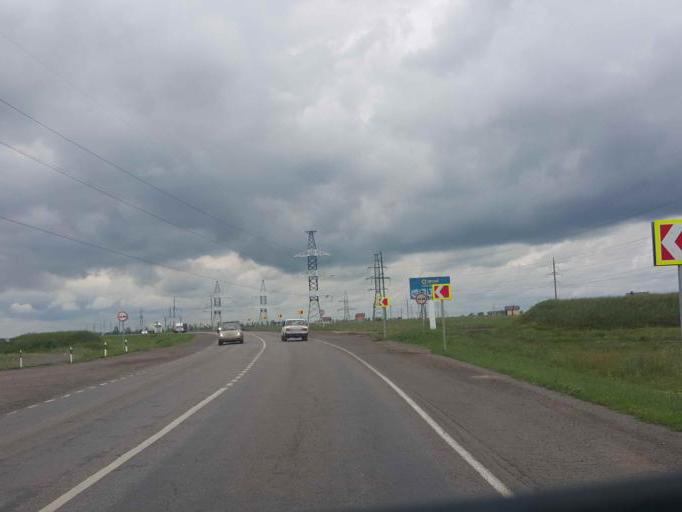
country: RU
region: Tambov
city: Komsomolets
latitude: 52.7813
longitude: 41.3513
